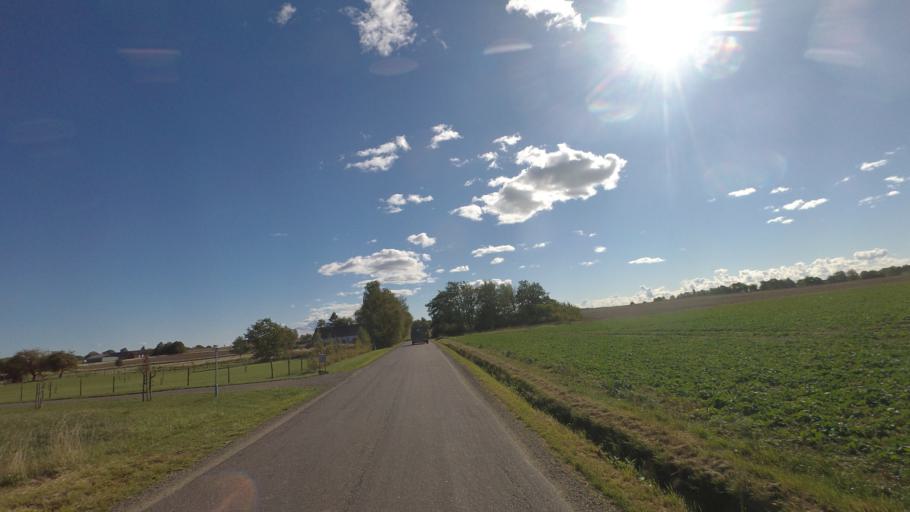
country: DK
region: Capital Region
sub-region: Bornholm Kommune
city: Akirkeby
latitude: 55.1294
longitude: 15.0244
